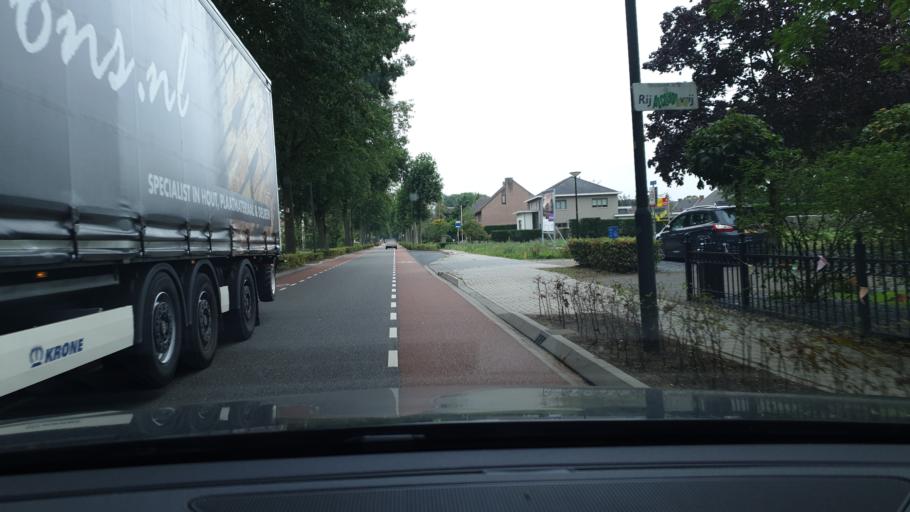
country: NL
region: North Brabant
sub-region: Gemeente Bladel en Netersel
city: Bladel
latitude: 51.3698
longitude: 5.2664
